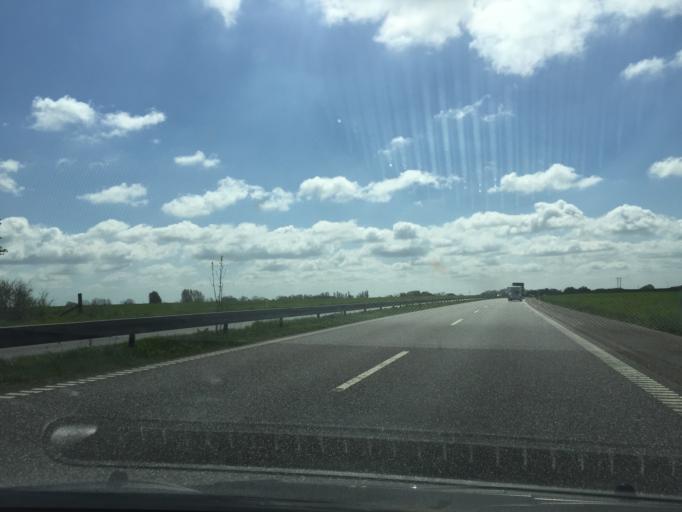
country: DK
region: Zealand
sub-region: Guldborgsund Kommune
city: Norre Alslev
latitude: 54.8788
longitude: 11.9028
